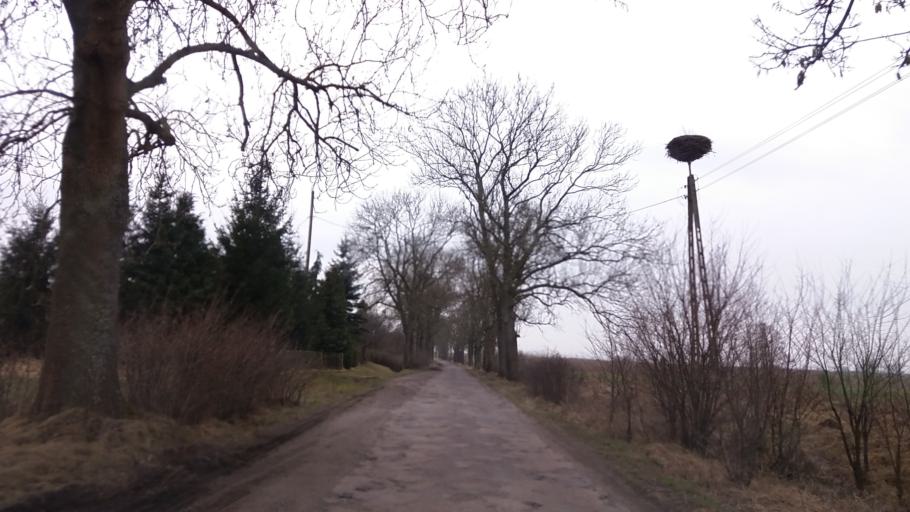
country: PL
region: West Pomeranian Voivodeship
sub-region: Powiat choszczenski
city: Bierzwnik
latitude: 53.0398
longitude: 15.7345
